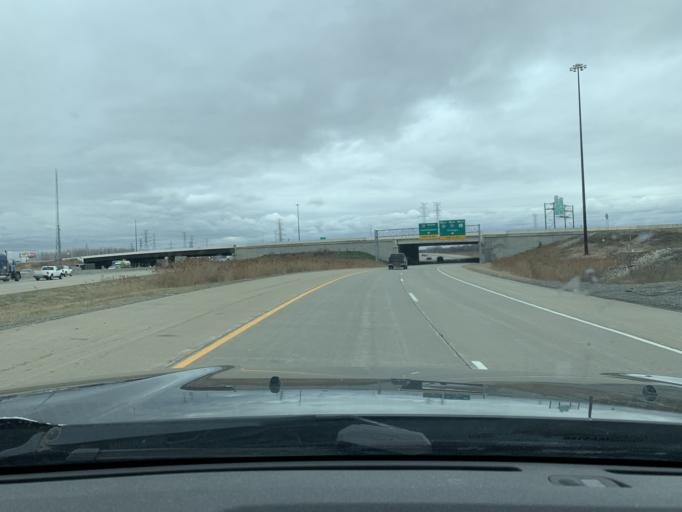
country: US
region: Indiana
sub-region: Lake County
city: New Chicago
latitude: 41.5702
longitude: -87.2974
